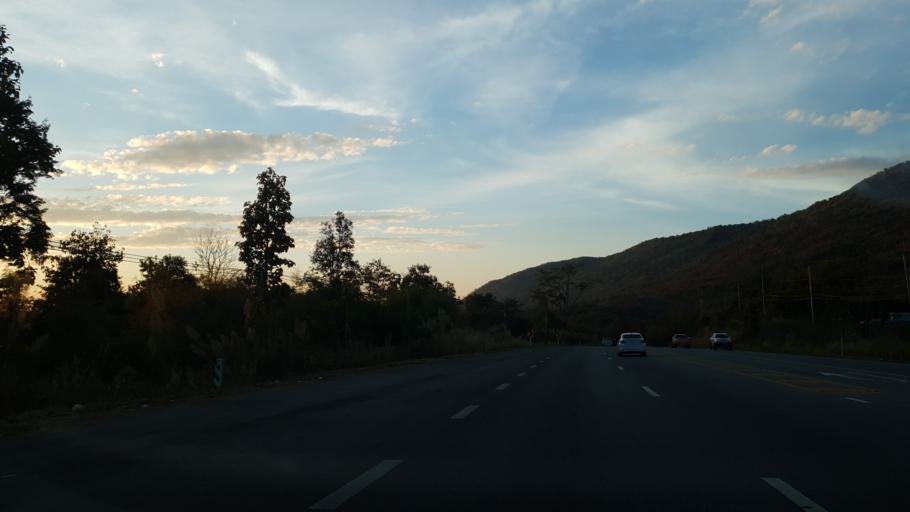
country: TH
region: Phitsanulok
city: Nakhon Thai
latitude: 16.8597
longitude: 100.7267
